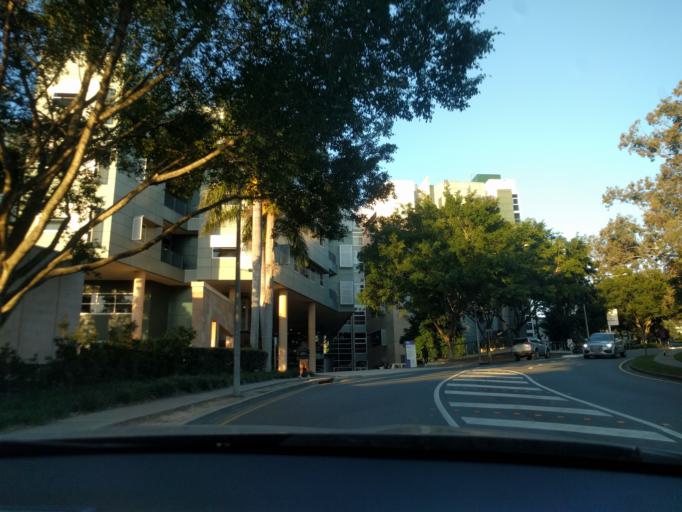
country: AU
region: Queensland
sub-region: Brisbane
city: Yeronga
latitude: -27.4984
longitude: 153.0093
